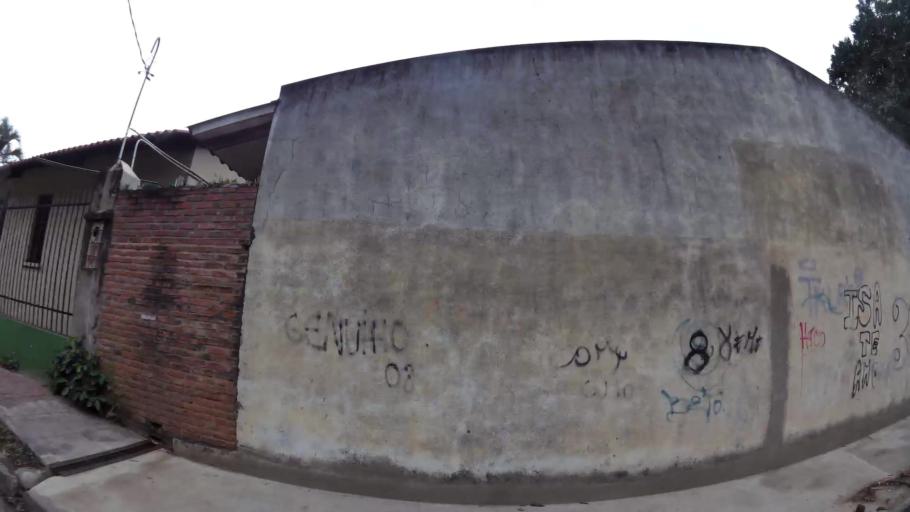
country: BO
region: Santa Cruz
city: Santa Cruz de la Sierra
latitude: -17.7815
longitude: -63.1624
